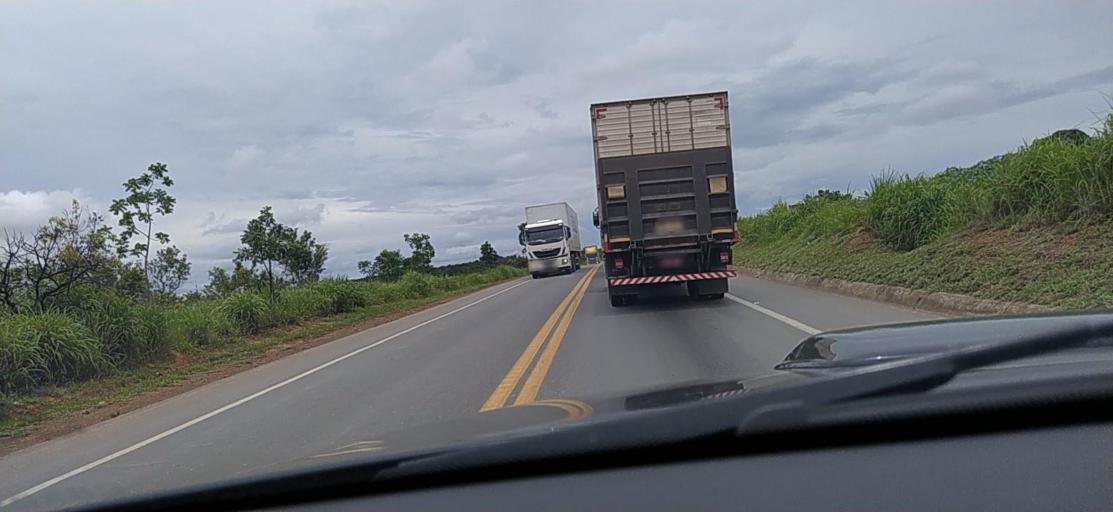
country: BR
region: Minas Gerais
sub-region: Curvelo
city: Curvelo
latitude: -18.7303
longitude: -44.4425
